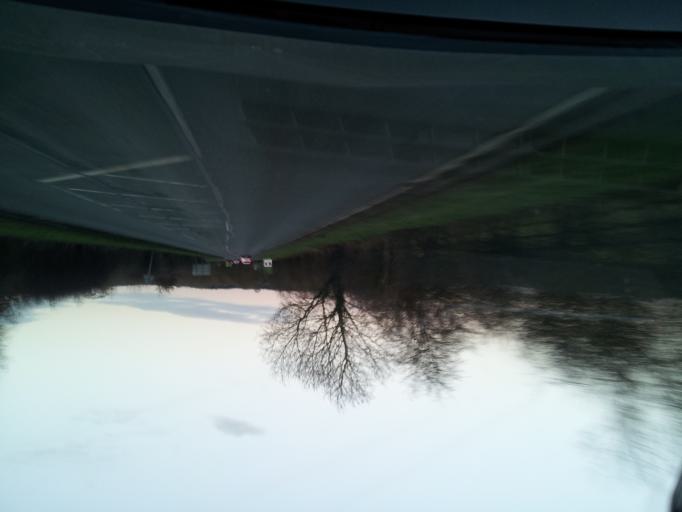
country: GB
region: England
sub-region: District of Rutland
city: Ridlington
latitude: 52.5975
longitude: -0.7910
